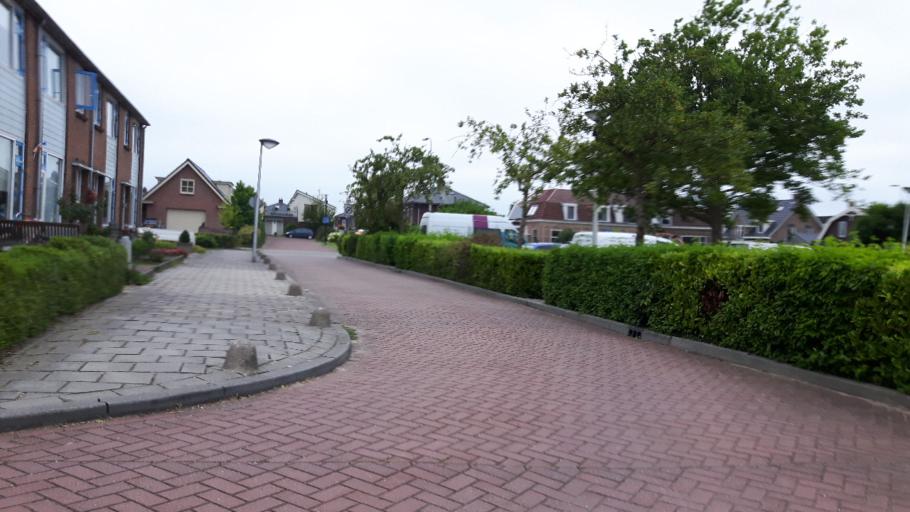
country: NL
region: South Holland
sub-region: Gemeente Kaag en Braassem
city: Oude Wetering
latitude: 52.1904
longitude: 4.6290
